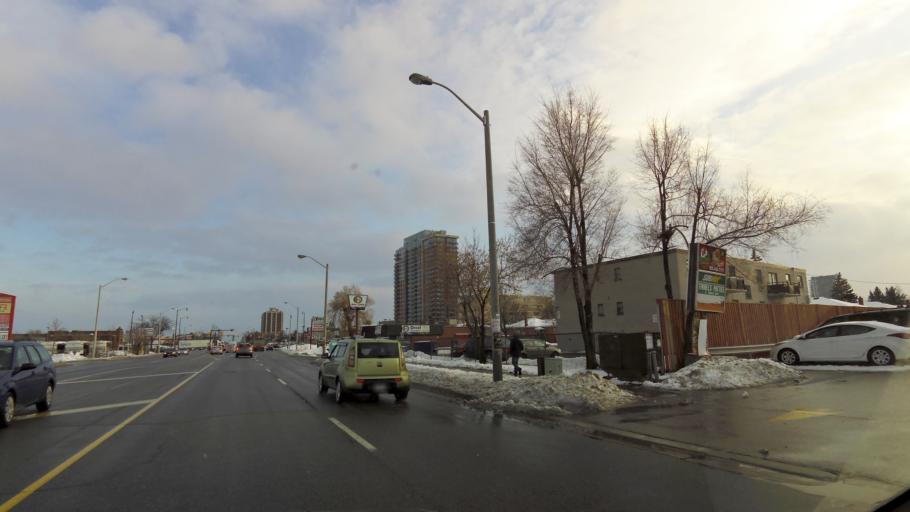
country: CA
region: Ontario
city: Brampton
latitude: 43.6970
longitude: -79.7513
